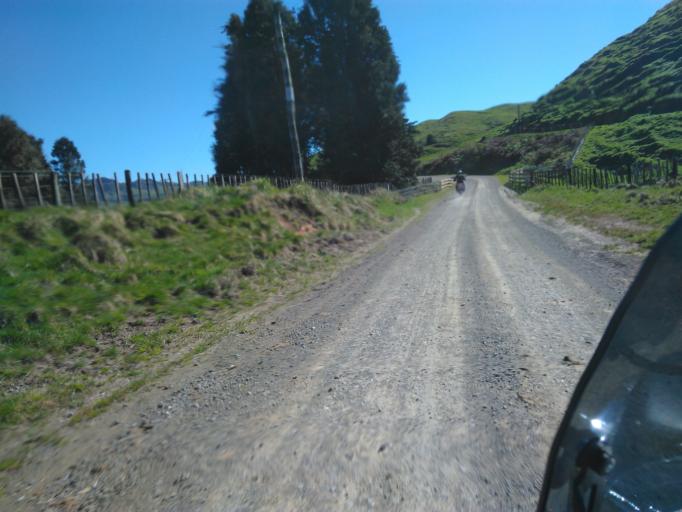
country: NZ
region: Bay of Plenty
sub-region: Opotiki District
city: Opotiki
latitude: -38.2856
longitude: 177.5430
